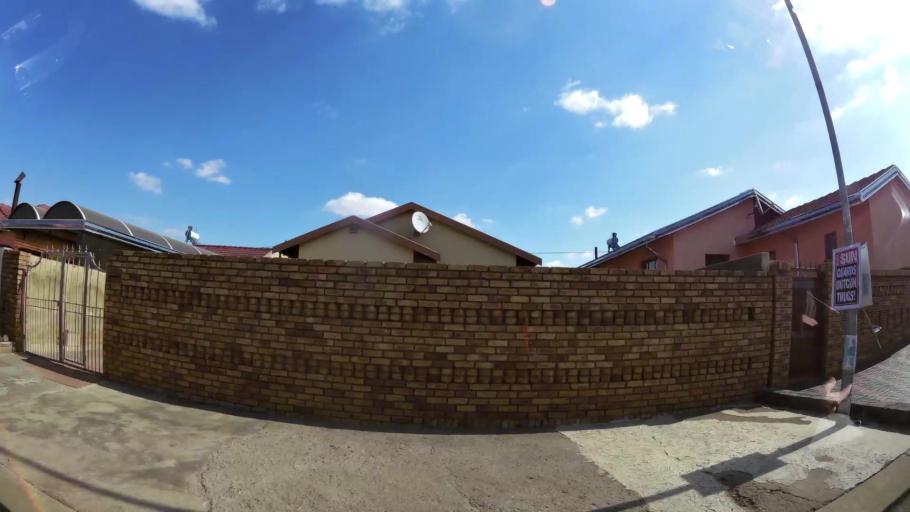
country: ZA
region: Gauteng
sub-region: West Rand District Municipality
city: Krugersdorp
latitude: -26.1642
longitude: 27.7878
